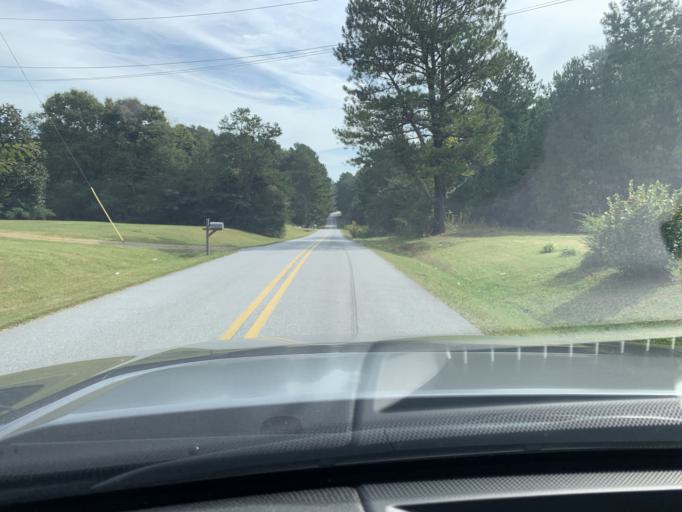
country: US
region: Georgia
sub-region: Polk County
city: Cedartown
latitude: 34.0644
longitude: -85.2411
